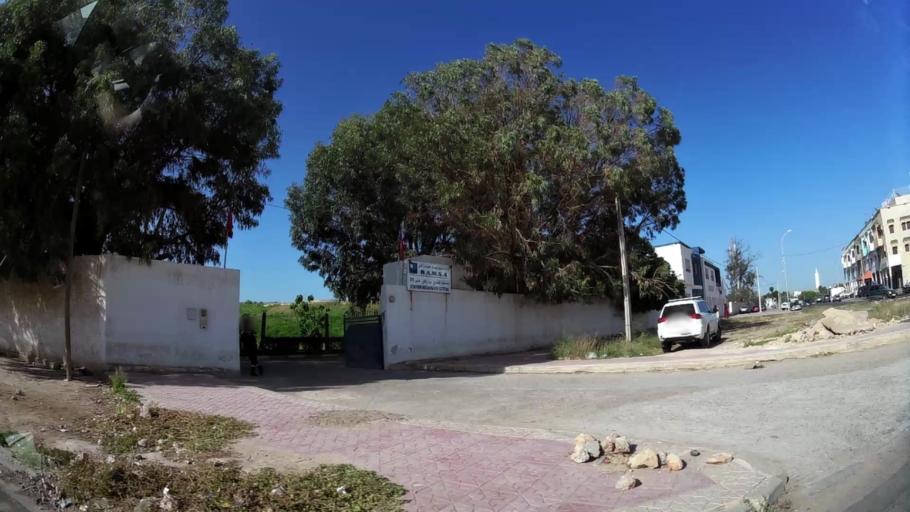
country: MA
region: Oued ed Dahab-Lagouira
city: Dakhla
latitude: 30.4239
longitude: -9.5720
